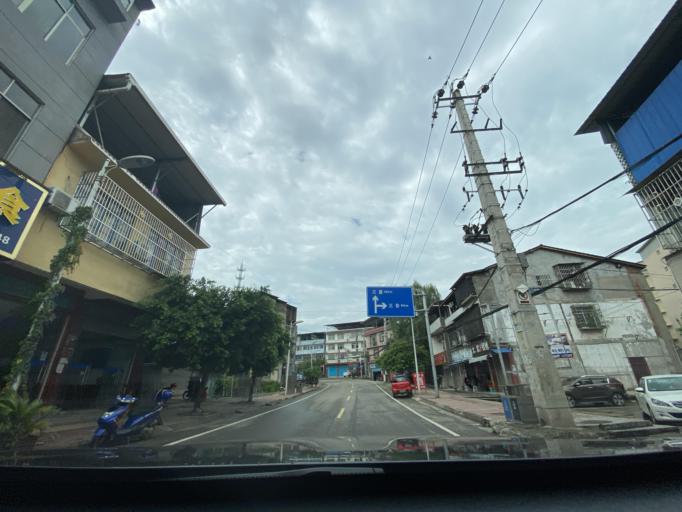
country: CN
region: Sichuan
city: Jiancheng
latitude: 30.4321
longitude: 104.6375
